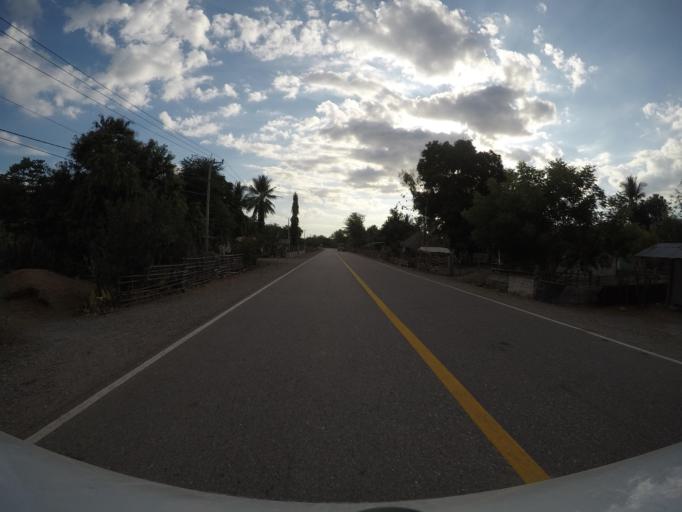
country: TL
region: Bobonaro
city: Maliana
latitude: -8.8678
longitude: 125.0441
